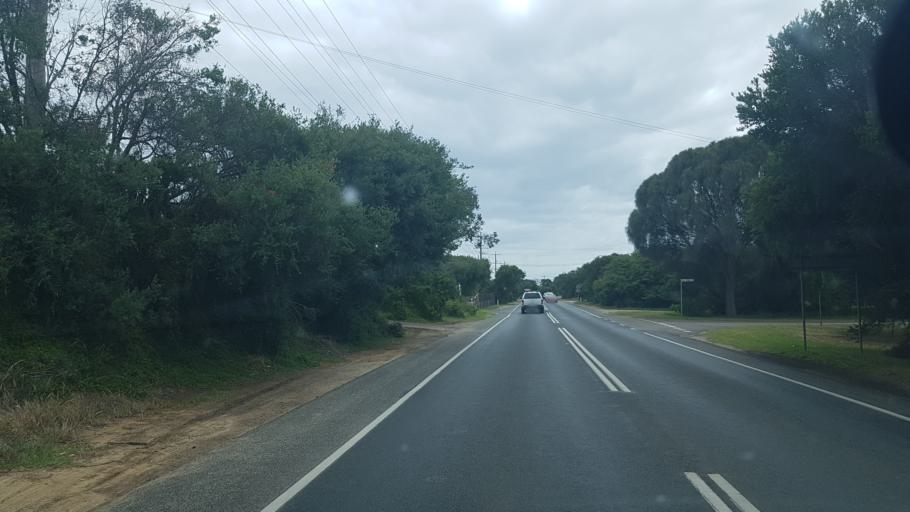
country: AU
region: Victoria
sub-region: Mornington Peninsula
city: Blairgowrie
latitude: -38.3791
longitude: 144.7845
